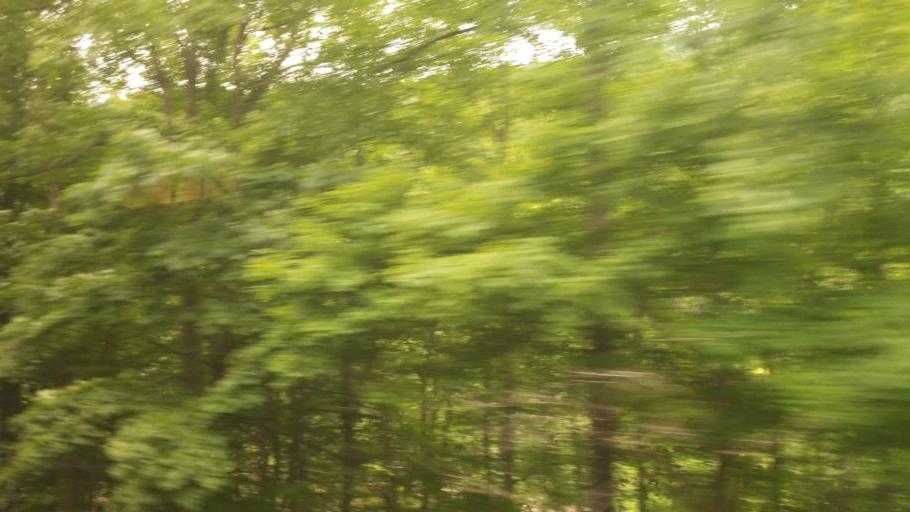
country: US
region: Pennsylvania
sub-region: Fayette County
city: South Connellsville
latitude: 39.8963
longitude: -79.4765
